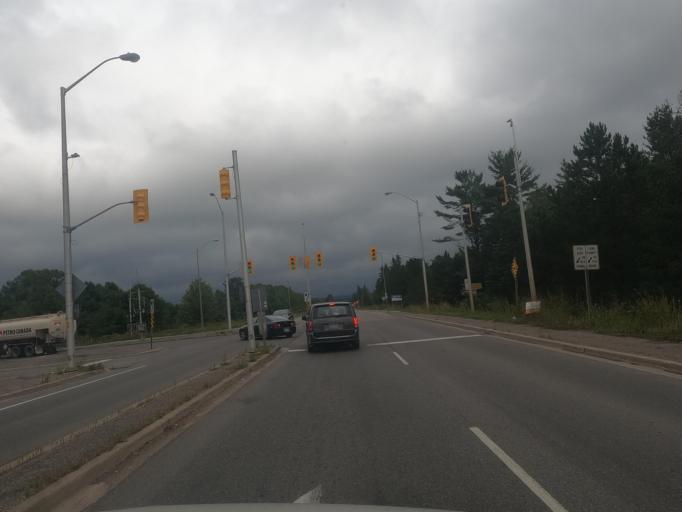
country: CA
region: Ontario
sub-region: Algoma
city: Sault Ste. Marie
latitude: 46.5409
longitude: -84.2302
